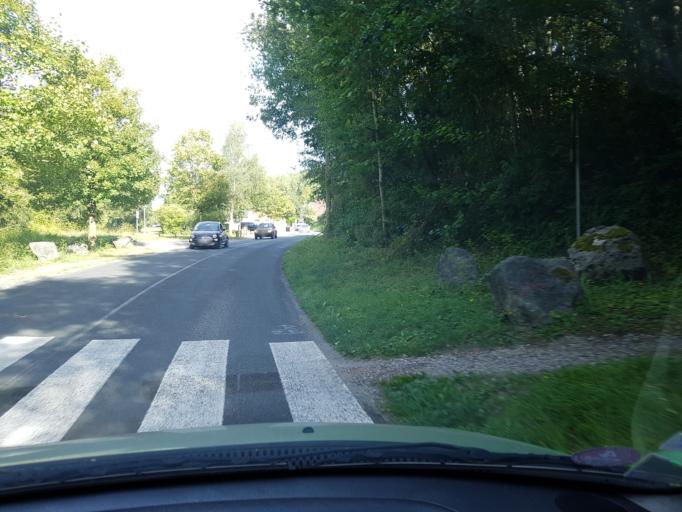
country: FR
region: Nord-Pas-de-Calais
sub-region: Departement du Pas-de-Calais
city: Lapugnoy
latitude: 50.5111
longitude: 2.5323
